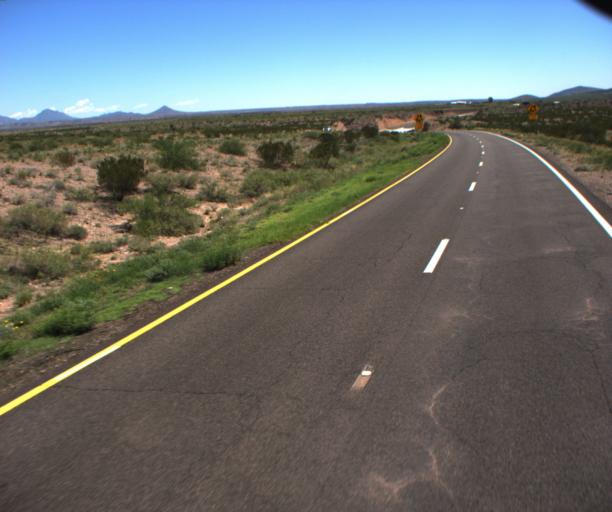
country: US
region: Arizona
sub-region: Greenlee County
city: Clifton
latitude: 32.9594
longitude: -109.2332
